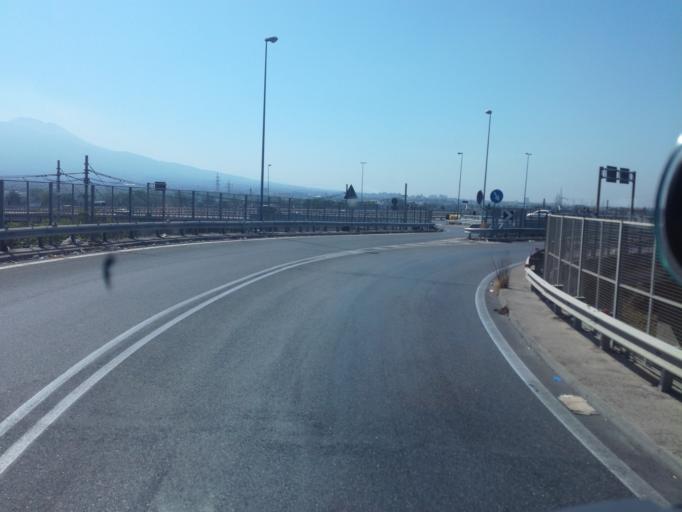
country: IT
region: Campania
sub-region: Provincia di Napoli
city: Arpino
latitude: 40.8919
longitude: 14.3271
